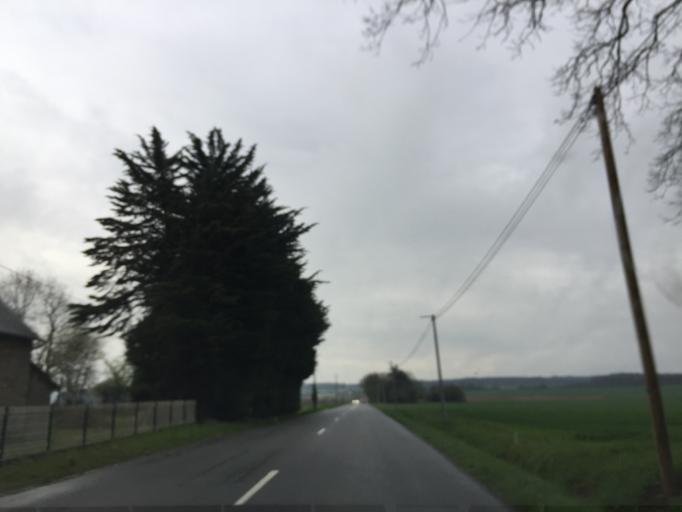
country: FR
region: Brittany
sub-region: Departement d'Ille-et-Vilaine
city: Martigne-Ferchaud
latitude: 47.8120
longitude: -1.2900
